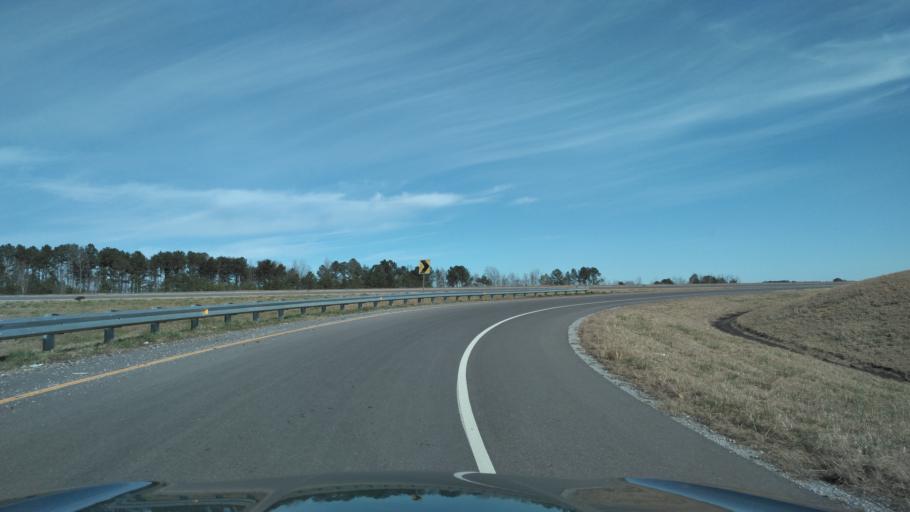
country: US
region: Alabama
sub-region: Walker County
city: Jasper
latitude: 33.8553
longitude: -87.3497
